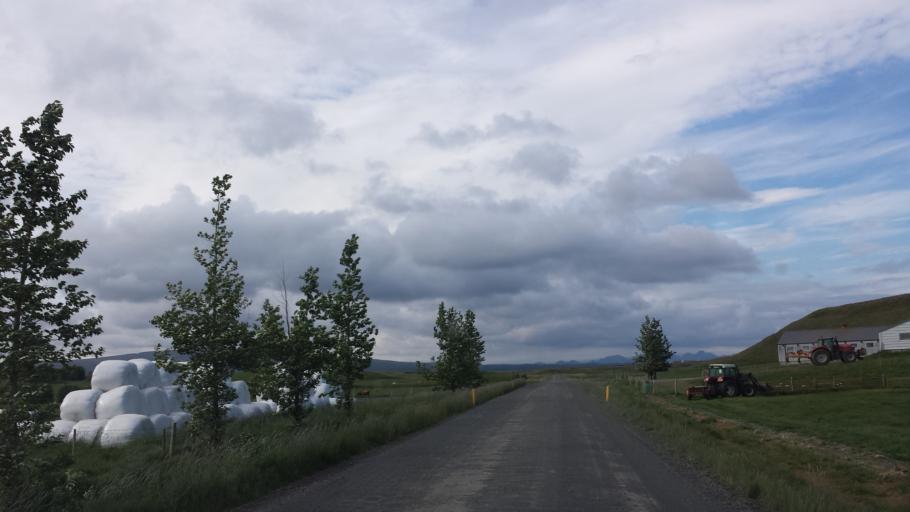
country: IS
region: South
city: Vestmannaeyjar
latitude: 64.2812
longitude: -20.2249
